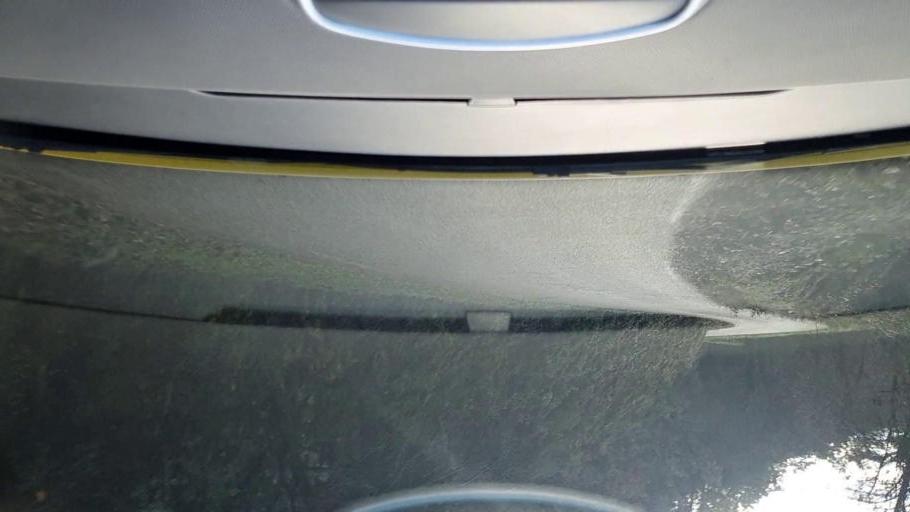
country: FR
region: Languedoc-Roussillon
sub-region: Departement du Gard
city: Branoux-les-Taillades
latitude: 44.2989
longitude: 3.9938
